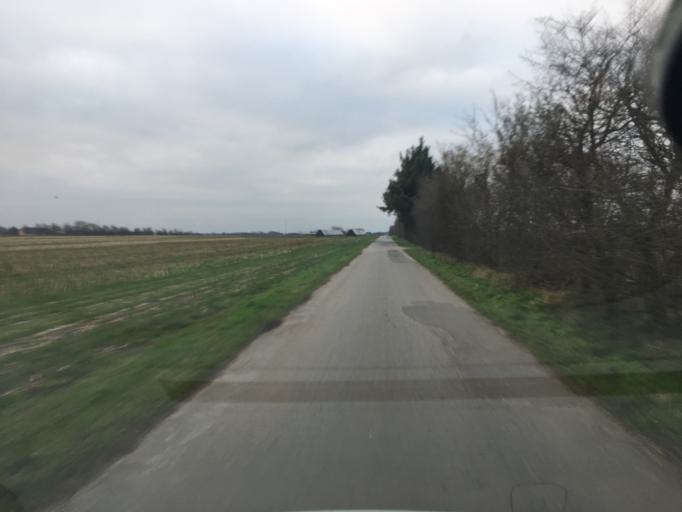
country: DK
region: South Denmark
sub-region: Tonder Kommune
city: Logumkloster
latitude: 55.0514
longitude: 9.0452
